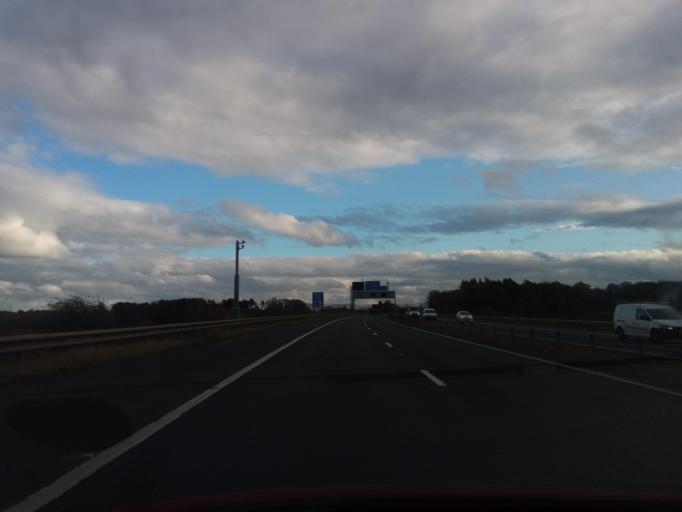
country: GB
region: Scotland
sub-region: West Lothian
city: Broxburn
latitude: 55.9674
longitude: -3.4503
